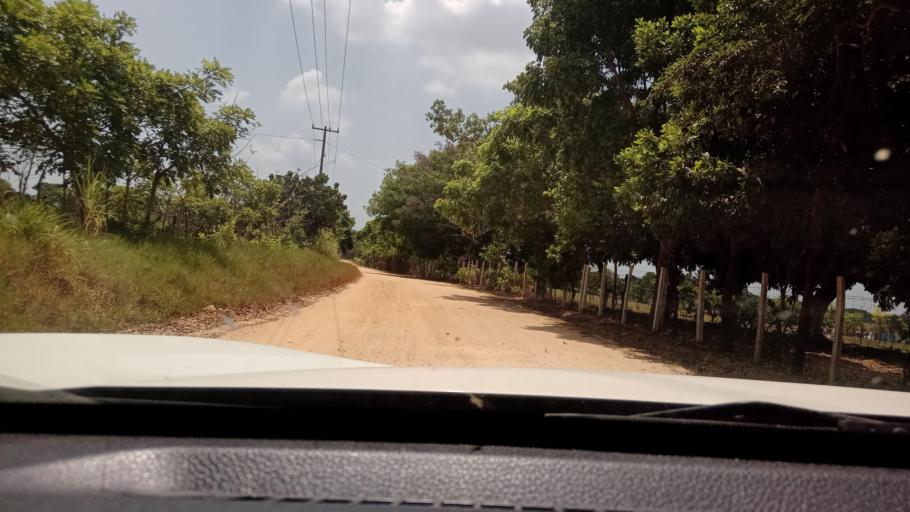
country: MX
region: Veracruz
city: Las Choapas
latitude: 17.9369
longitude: -94.1177
